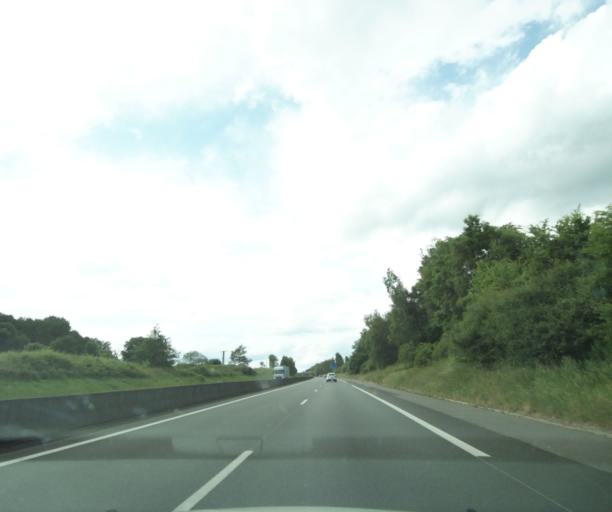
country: FR
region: Centre
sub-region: Departement du Cher
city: Vierzon
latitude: 47.2298
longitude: 2.1015
